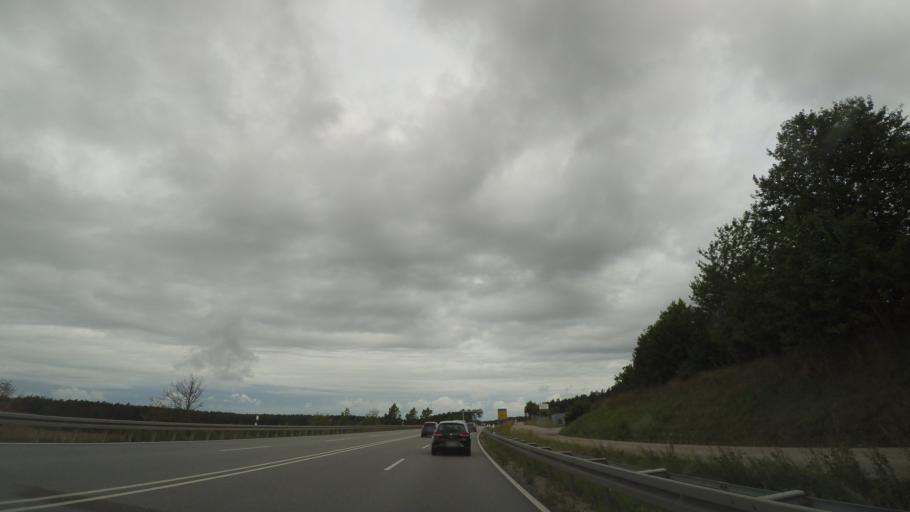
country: DE
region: Bavaria
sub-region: Upper Palatinate
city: Breitenbrunn
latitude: 49.3752
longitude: 12.0250
